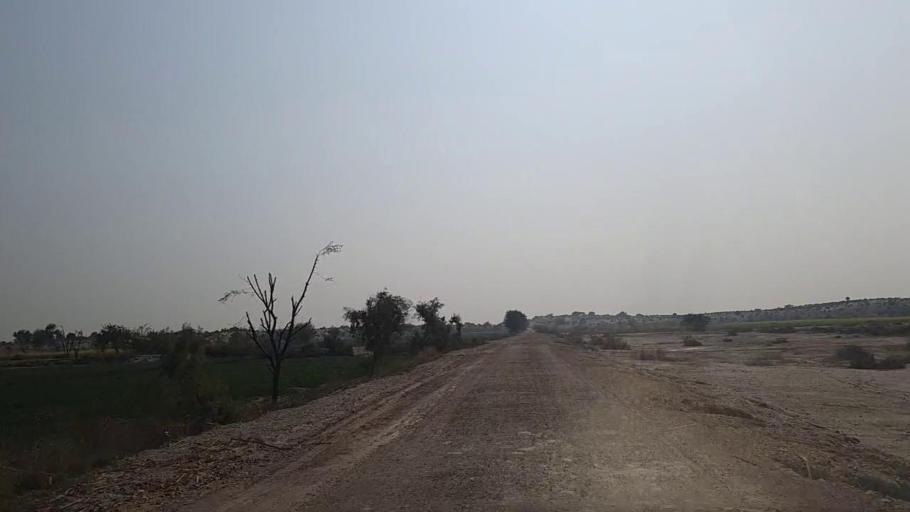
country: PK
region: Sindh
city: Jam Sahib
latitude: 26.4504
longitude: 68.5233
